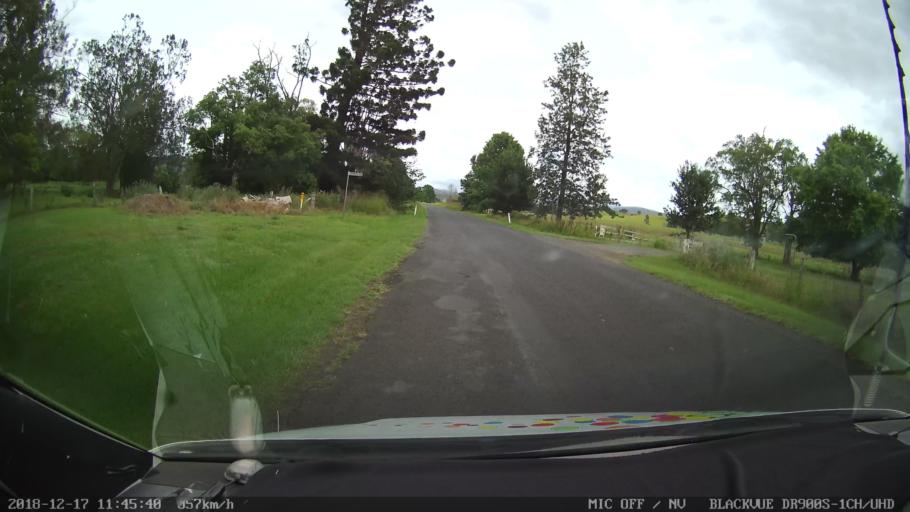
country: AU
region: New South Wales
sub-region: Kyogle
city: Kyogle
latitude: -28.6428
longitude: 152.5974
